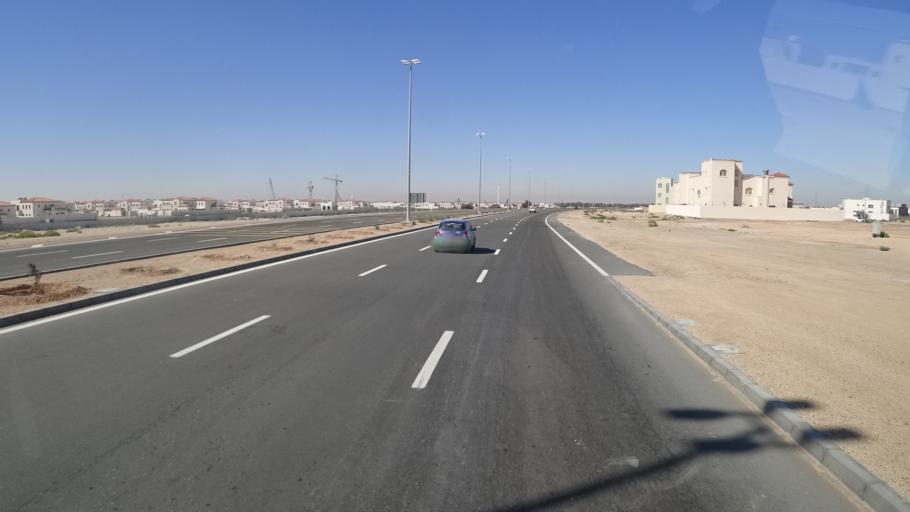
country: AE
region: Abu Dhabi
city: Al Ain
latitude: 24.0999
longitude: 55.7050
